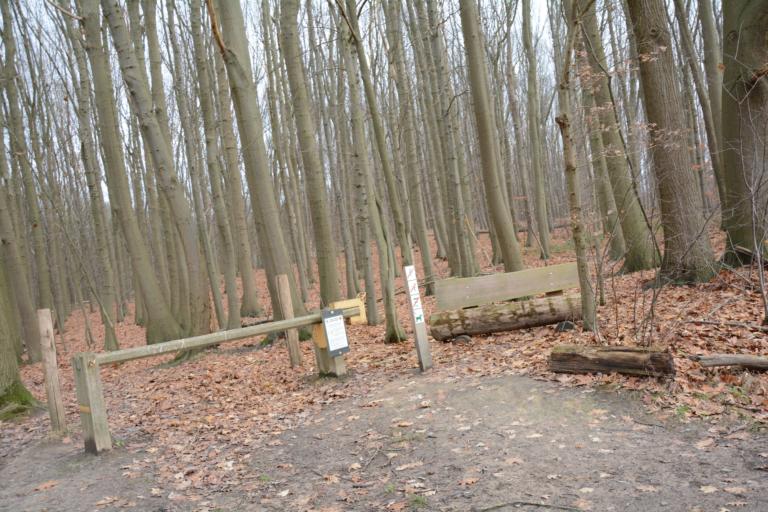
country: BE
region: Flanders
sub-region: Provincie Vlaams-Brabant
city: Opwijk
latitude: 50.9318
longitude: 4.1489
